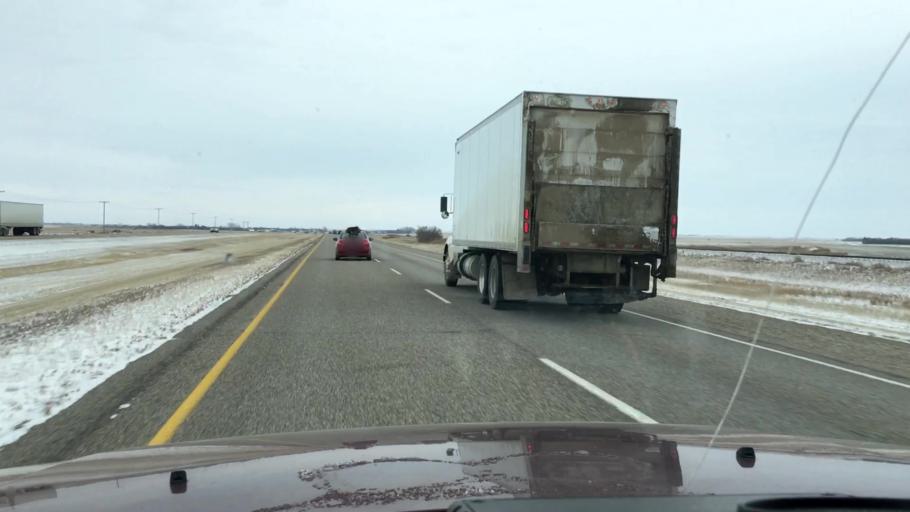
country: CA
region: Saskatchewan
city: Watrous
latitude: 51.1786
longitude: -105.9376
